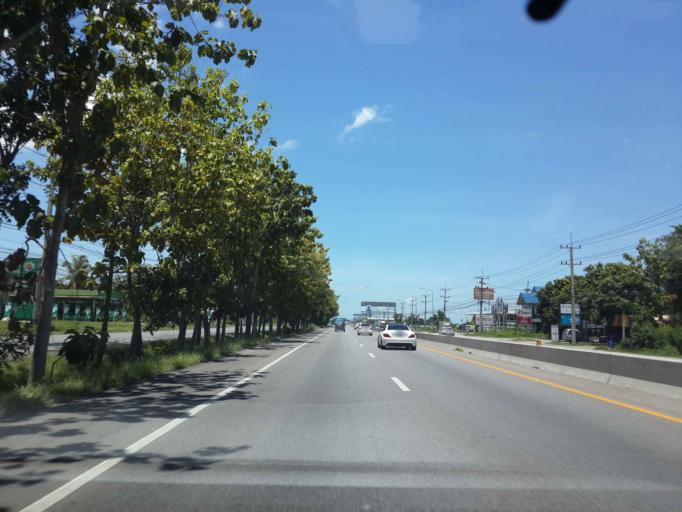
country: TH
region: Ratchaburi
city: Pak Tho
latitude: 13.3204
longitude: 99.8275
